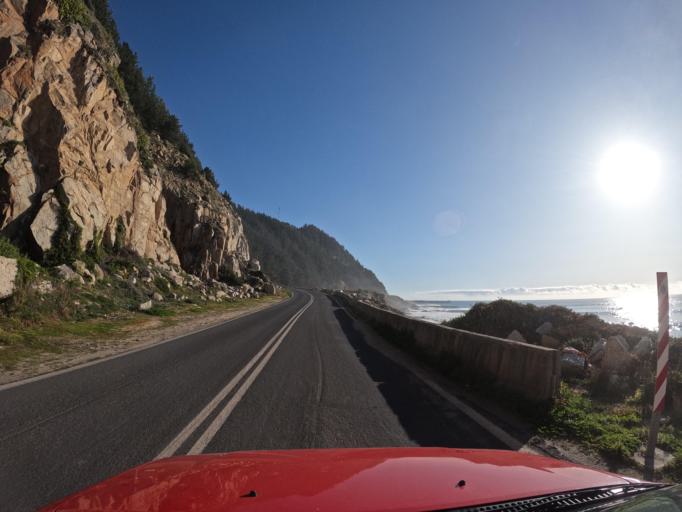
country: CL
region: Maule
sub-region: Provincia de Talca
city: Constitucion
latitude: -35.3514
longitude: -72.4441
